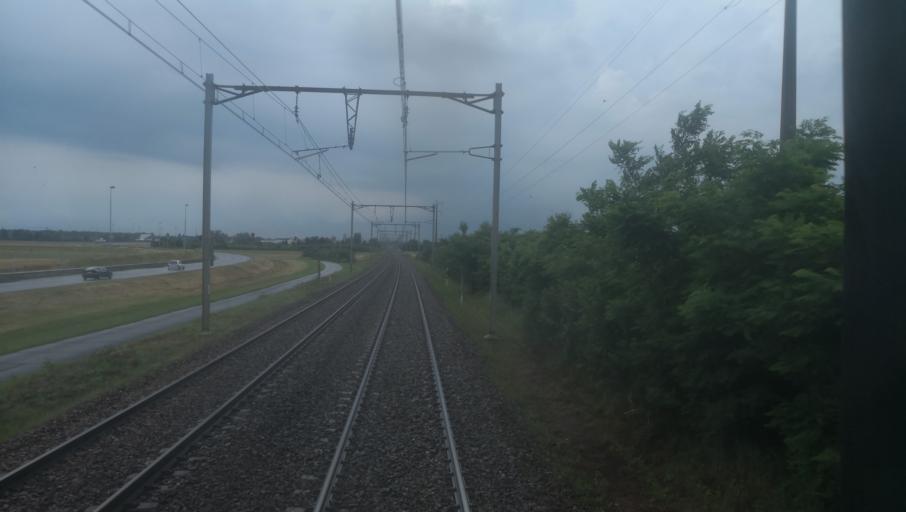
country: FR
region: Centre
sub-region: Departement du Loiret
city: Saint-Denis-en-Val
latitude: 47.8527
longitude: 1.9430
